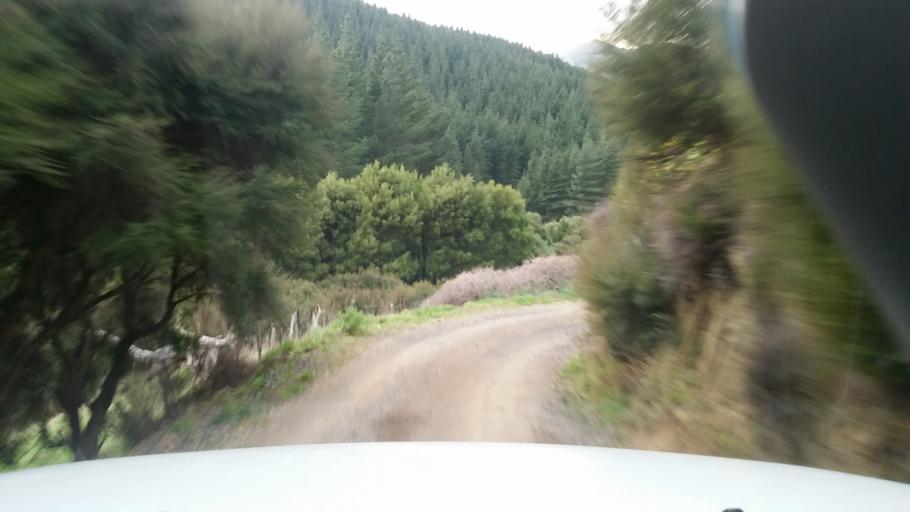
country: NZ
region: Canterbury
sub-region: Christchurch City
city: Christchurch
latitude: -43.7235
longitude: 172.7796
